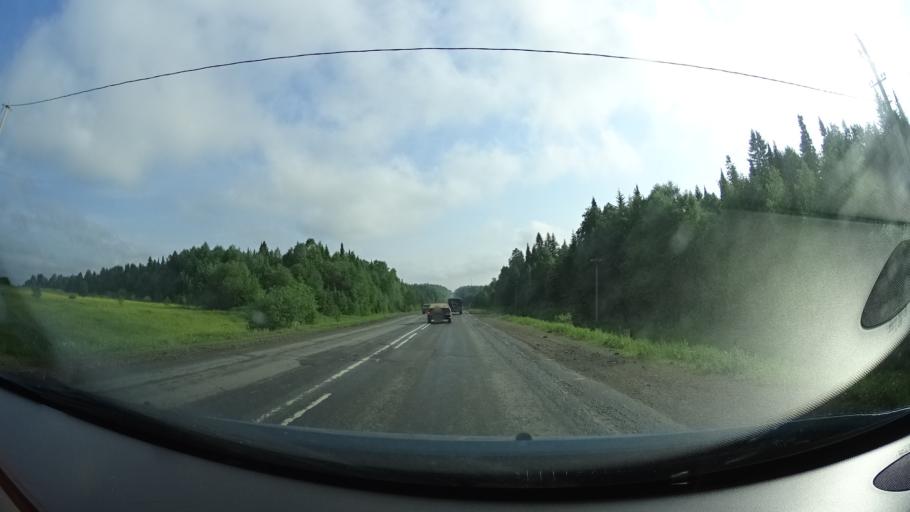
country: RU
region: Perm
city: Kultayevo
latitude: 57.8270
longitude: 55.8098
